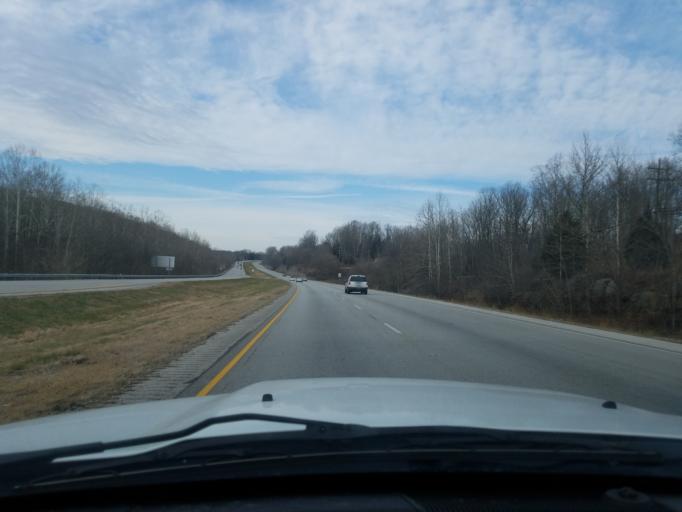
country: US
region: Indiana
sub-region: Lawrence County
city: Oolitic
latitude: 38.9022
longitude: -86.5333
